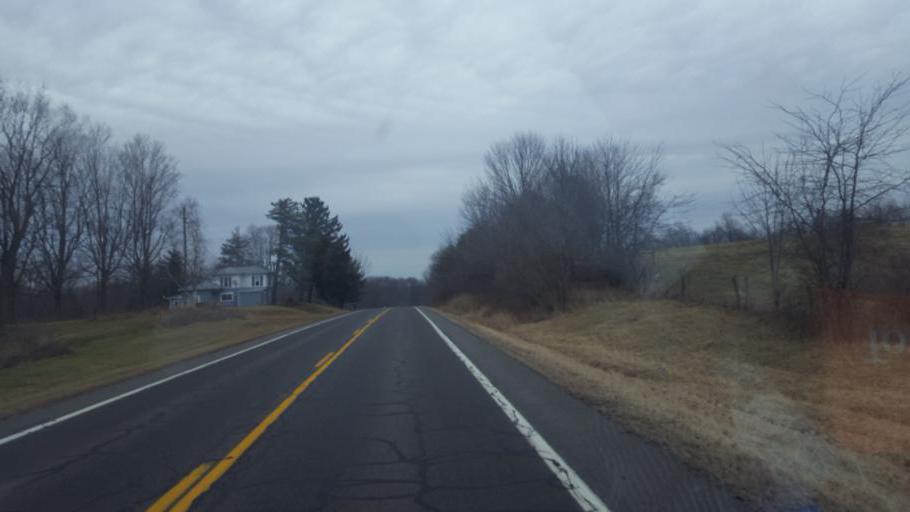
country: US
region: Ohio
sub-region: Crawford County
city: Galion
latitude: 40.6722
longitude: -82.8210
